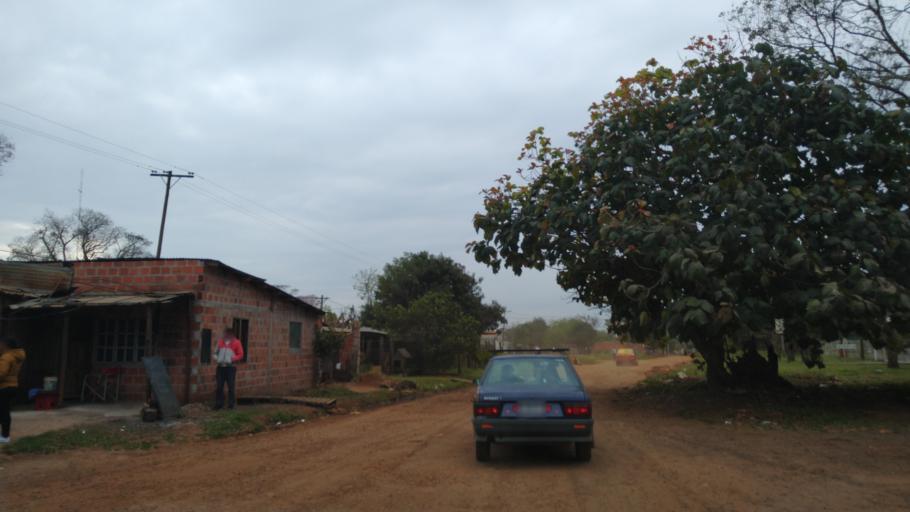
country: AR
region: Misiones
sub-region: Departamento de Capital
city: Posadas
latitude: -27.4258
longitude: -55.8949
